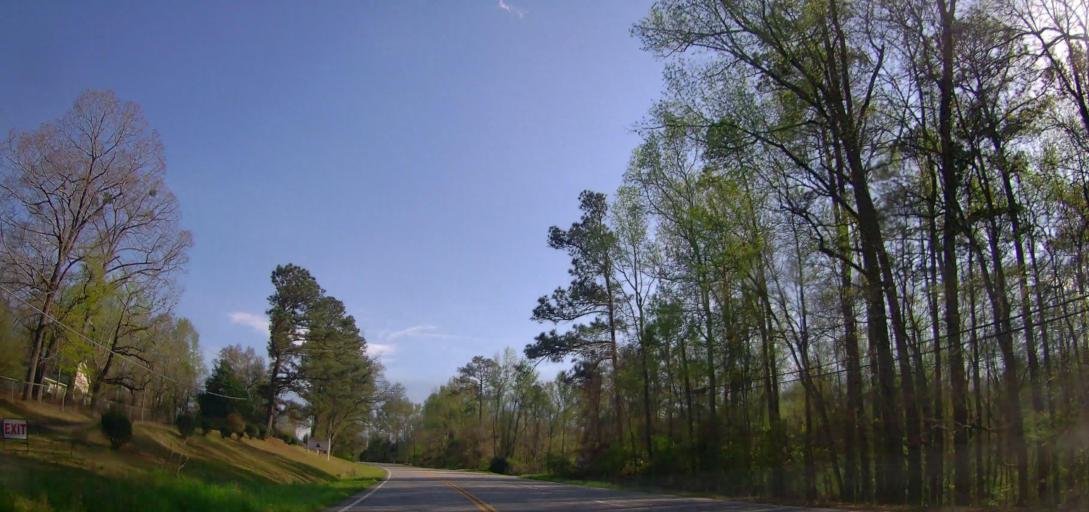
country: US
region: Georgia
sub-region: Baldwin County
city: Hardwick
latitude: 33.0319
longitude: -83.2363
